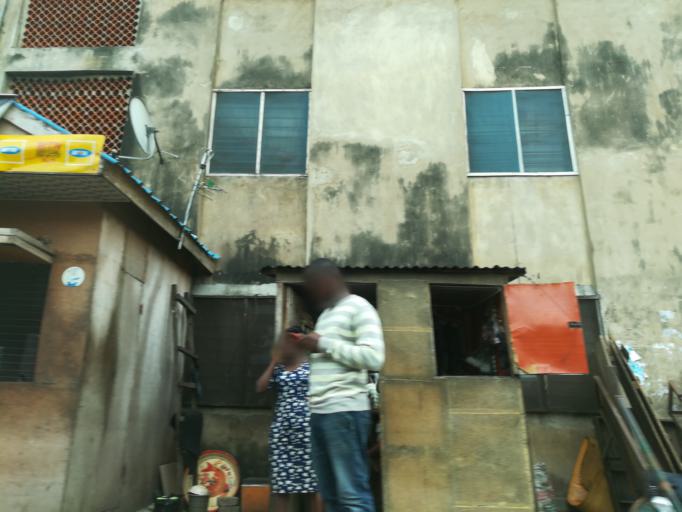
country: NG
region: Lagos
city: Ojota
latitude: 6.6107
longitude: 3.3976
